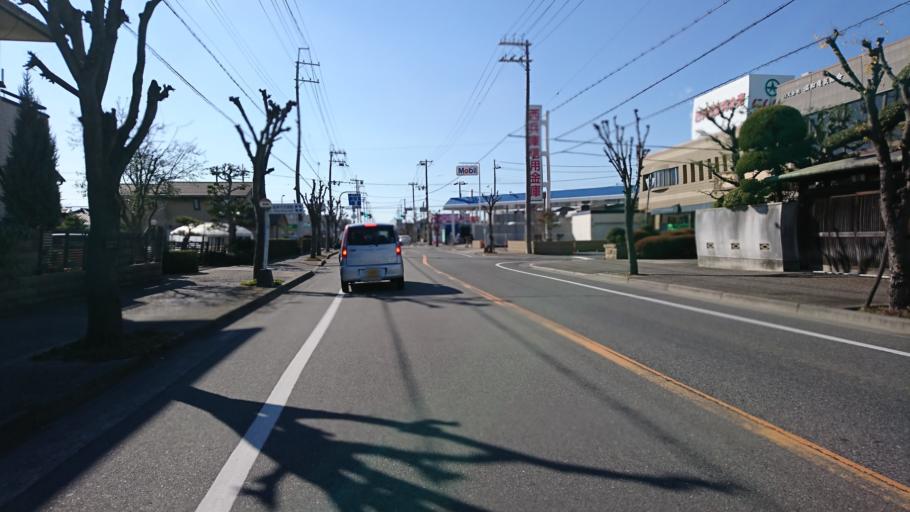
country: JP
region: Hyogo
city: Kakogawacho-honmachi
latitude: 34.7645
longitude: 134.7971
